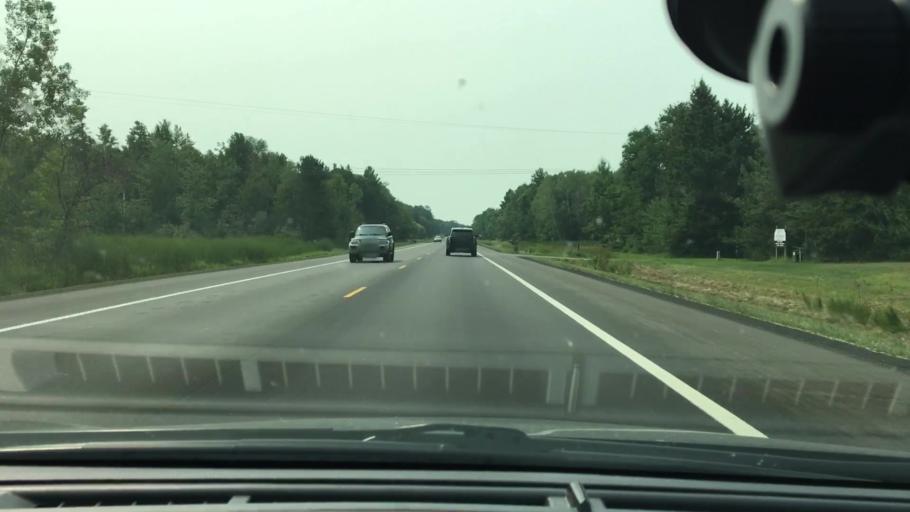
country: US
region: Minnesota
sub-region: Crow Wing County
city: Brainerd
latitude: 46.4461
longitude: -94.1719
